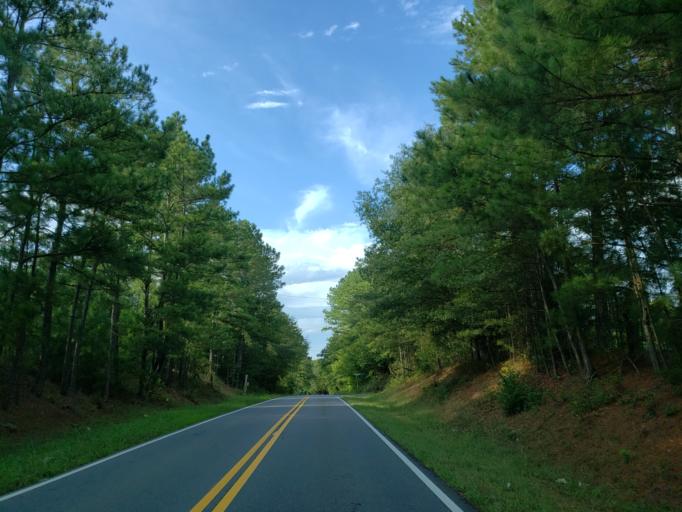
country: US
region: Georgia
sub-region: Bartow County
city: Euharlee
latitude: 34.1903
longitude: -84.9843
